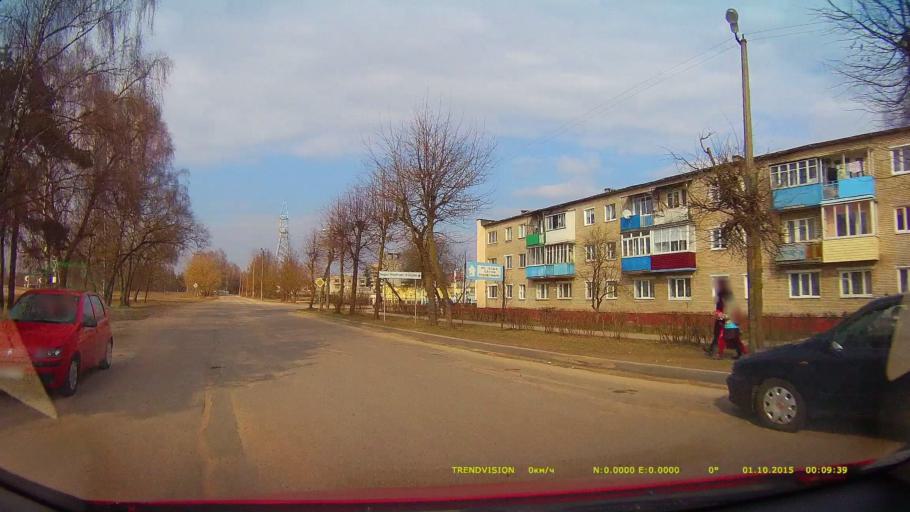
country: BY
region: Grodnenskaya
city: Lida
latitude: 53.9358
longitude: 25.2633
